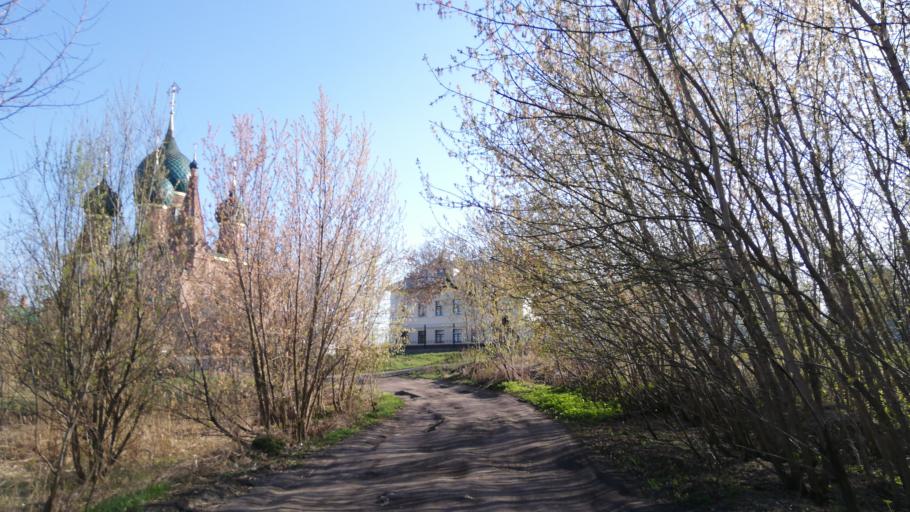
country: RU
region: Jaroslavl
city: Yaroslavl
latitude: 57.6126
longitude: 39.9061
